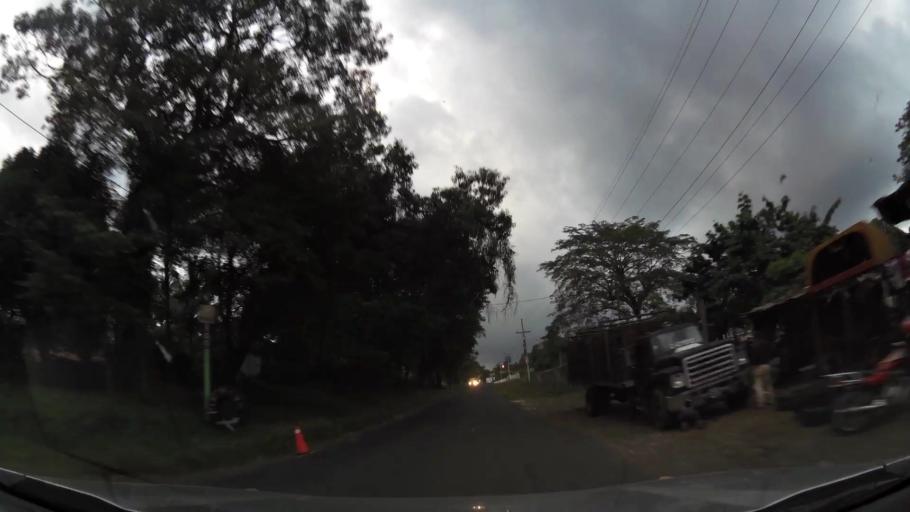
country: GT
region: Escuintla
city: Santa Lucia Cotzumalguapa
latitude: 14.3118
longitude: -91.0434
